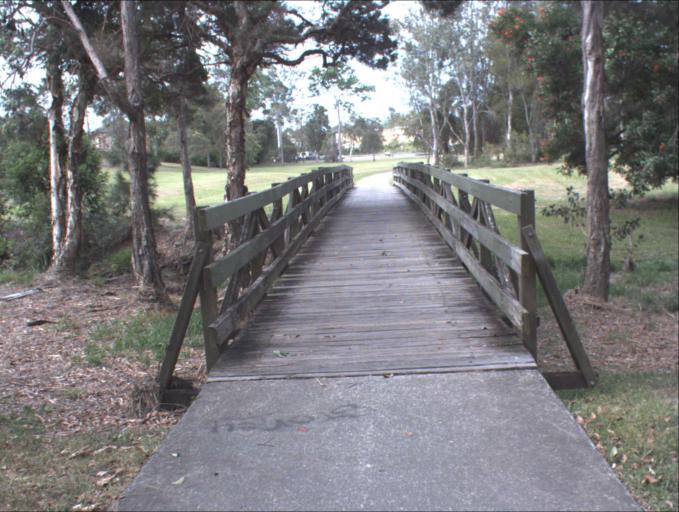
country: AU
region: Queensland
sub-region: Logan
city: Springwood
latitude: -27.6289
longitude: 153.1253
